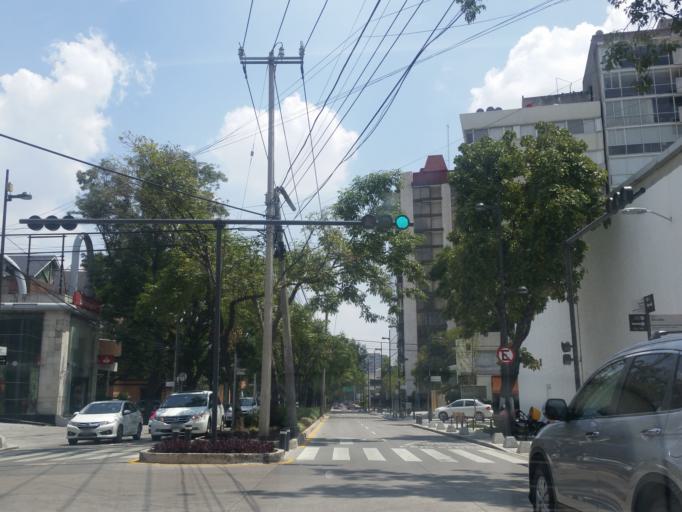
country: MX
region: Mexico City
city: Miguel Hidalgo
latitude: 19.4323
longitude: -99.2043
